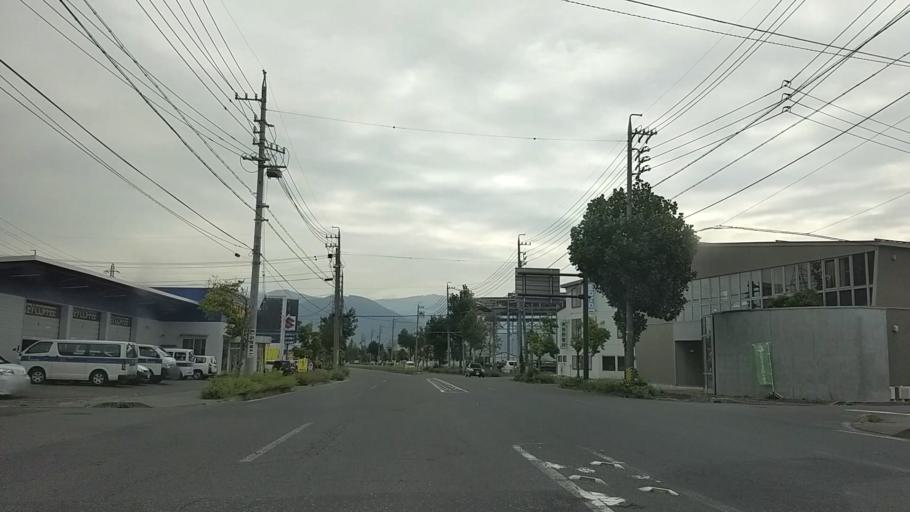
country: JP
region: Nagano
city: Nagano-shi
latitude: 36.6143
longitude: 138.1981
